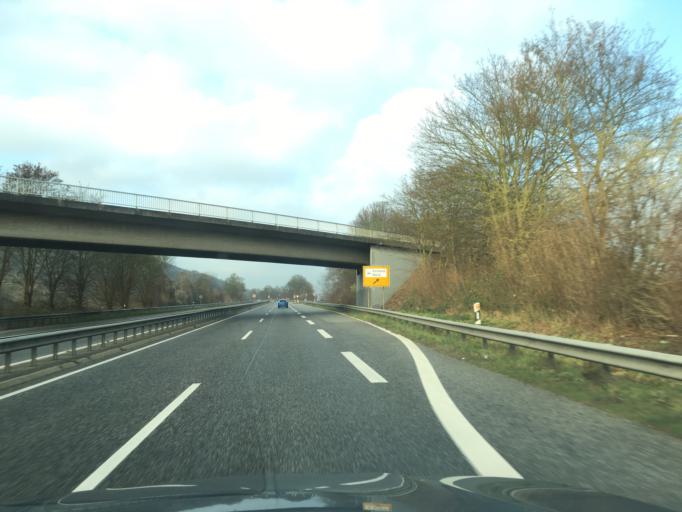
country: DE
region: Rheinland-Pfalz
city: Bad Breisig
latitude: 50.5247
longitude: 7.2836
